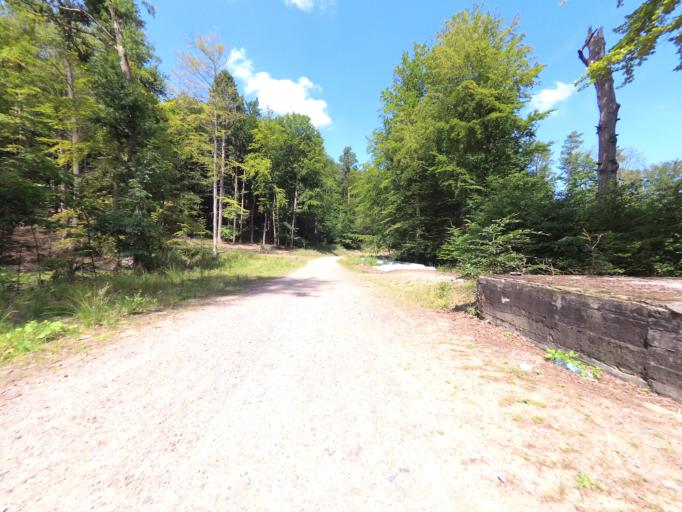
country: PL
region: Pomeranian Voivodeship
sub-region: Gdynia
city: Wielki Kack
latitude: 54.4836
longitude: 18.5004
